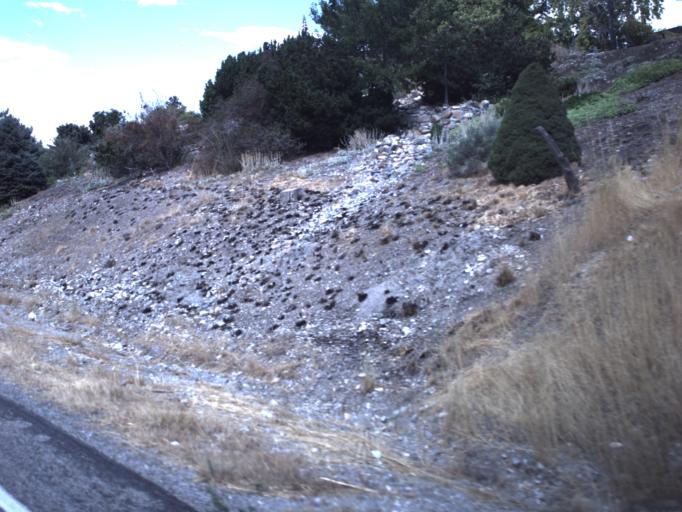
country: US
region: Utah
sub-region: Box Elder County
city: Elwood
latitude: 41.7368
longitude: -112.0986
